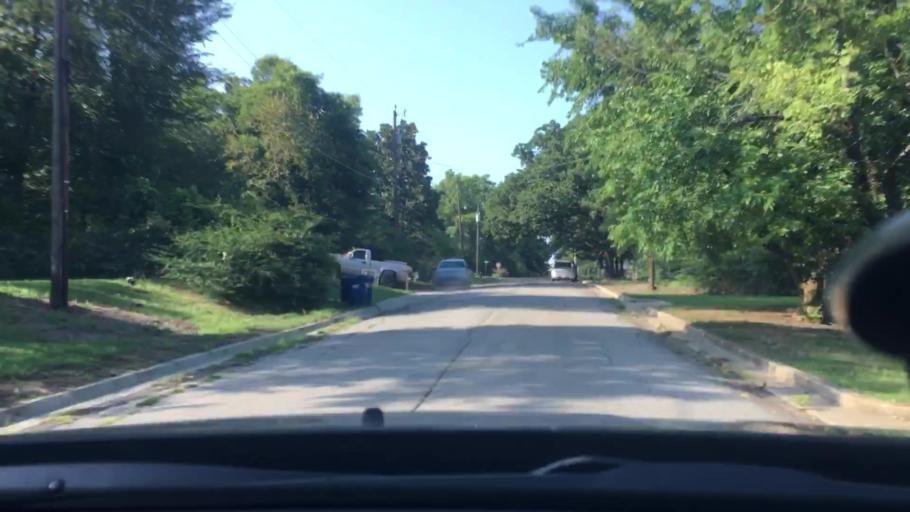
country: US
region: Oklahoma
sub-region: Atoka County
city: Atoka
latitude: 34.3881
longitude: -96.1312
